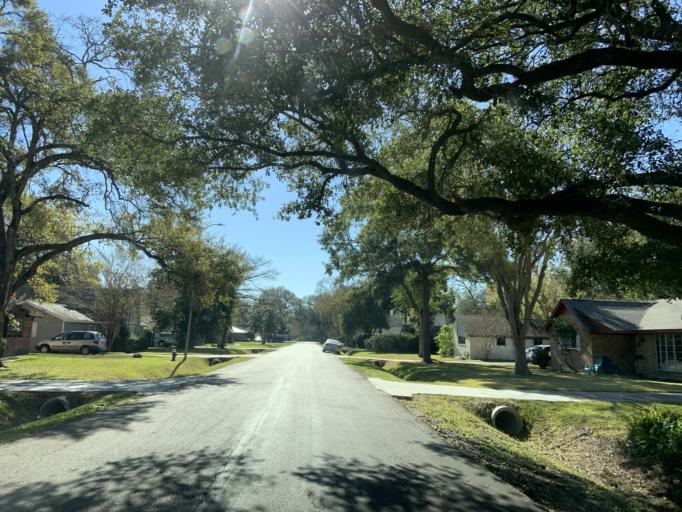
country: US
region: Texas
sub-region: Harris County
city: Bellaire
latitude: 29.6801
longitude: -95.5118
